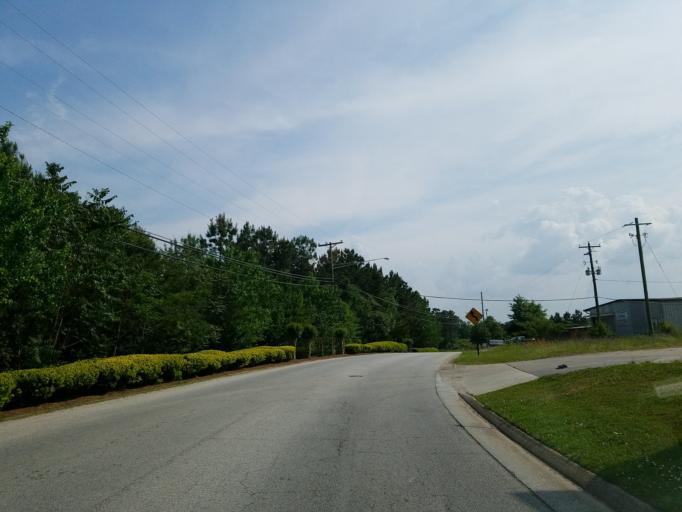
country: US
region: Georgia
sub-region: Paulding County
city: Dallas
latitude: 33.9089
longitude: -84.8030
